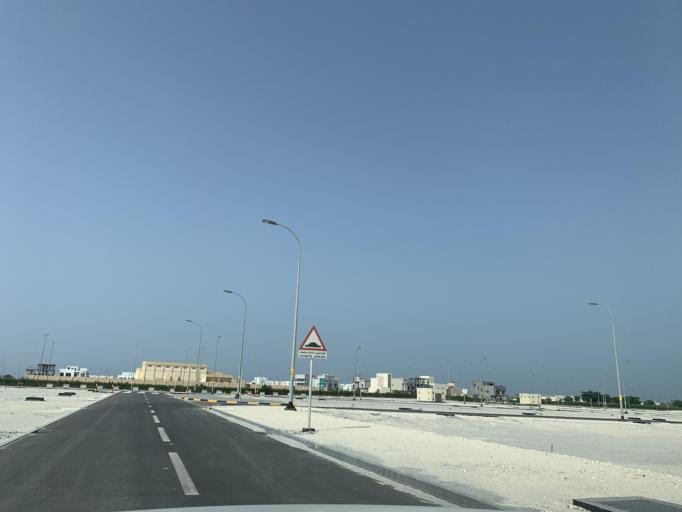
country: BH
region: Muharraq
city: Al Muharraq
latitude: 26.3078
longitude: 50.6310
